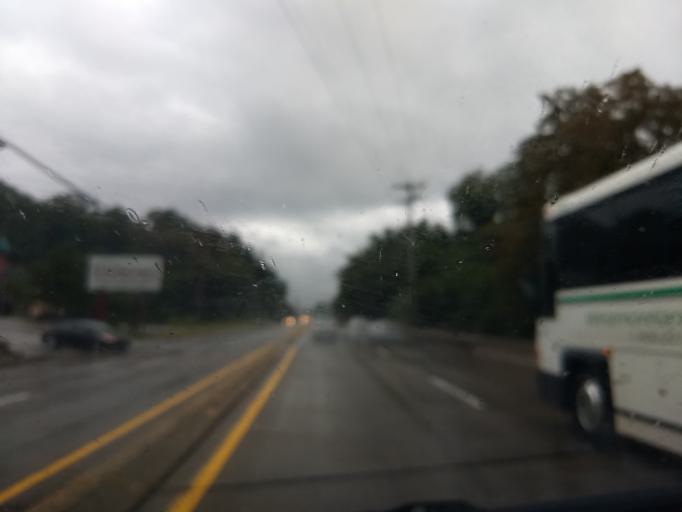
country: US
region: Pennsylvania
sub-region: Allegheny County
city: East Pittsburgh
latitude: 40.3875
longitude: -79.8286
